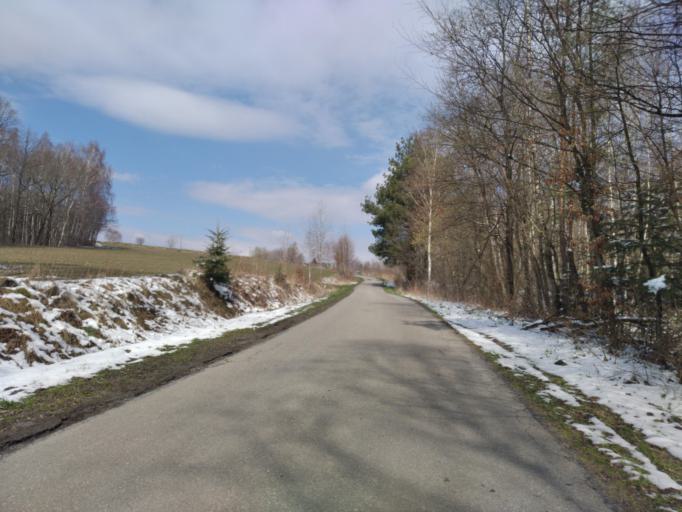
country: PL
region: Subcarpathian Voivodeship
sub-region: Powiat ropczycko-sedziszowski
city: Ropczyce
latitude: 50.0035
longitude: 21.5963
